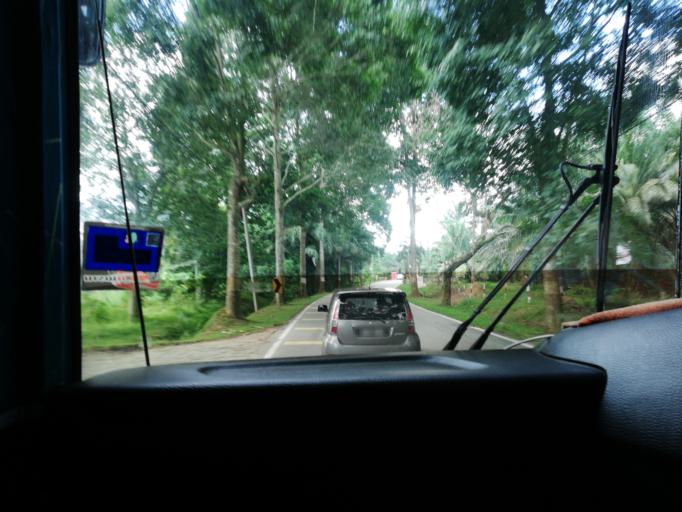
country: MY
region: Kedah
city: Kulim
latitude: 5.2479
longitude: 100.6027
